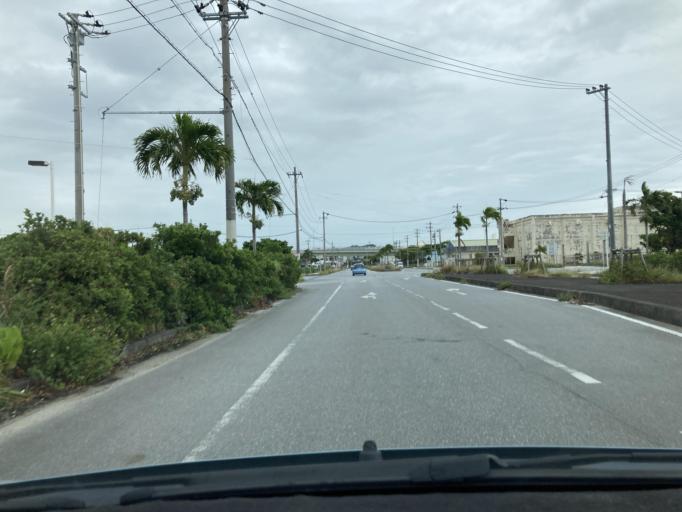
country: JP
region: Okinawa
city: Itoman
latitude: 26.1374
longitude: 127.6599
